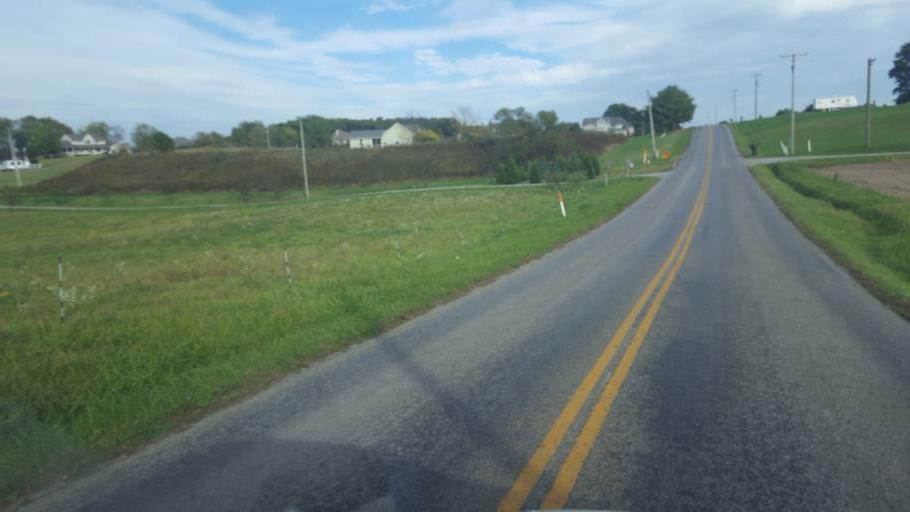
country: US
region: Ohio
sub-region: Holmes County
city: Millersburg
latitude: 40.5739
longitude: -81.8311
